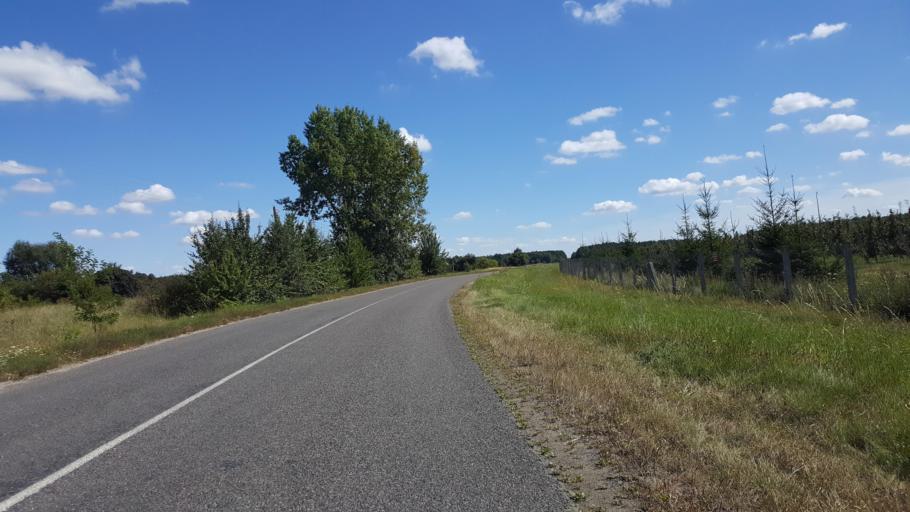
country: BY
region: Brest
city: Vysokaye
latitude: 52.2730
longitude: 23.3721
